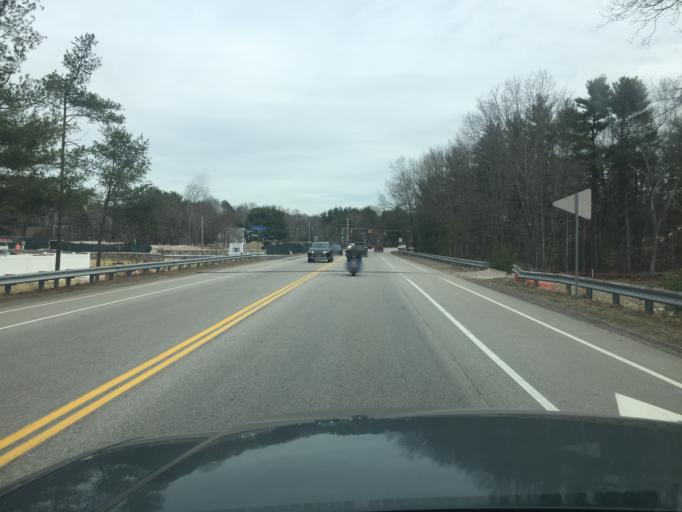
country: US
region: Massachusetts
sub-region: Norfolk County
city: Medfield
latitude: 42.1895
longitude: -71.3162
